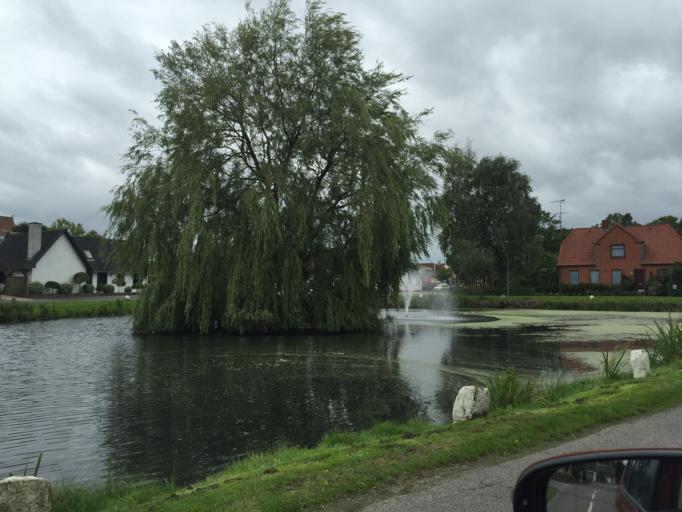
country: DK
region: South Denmark
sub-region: Assens Kommune
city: Arup
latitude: 55.3630
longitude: 10.0480
